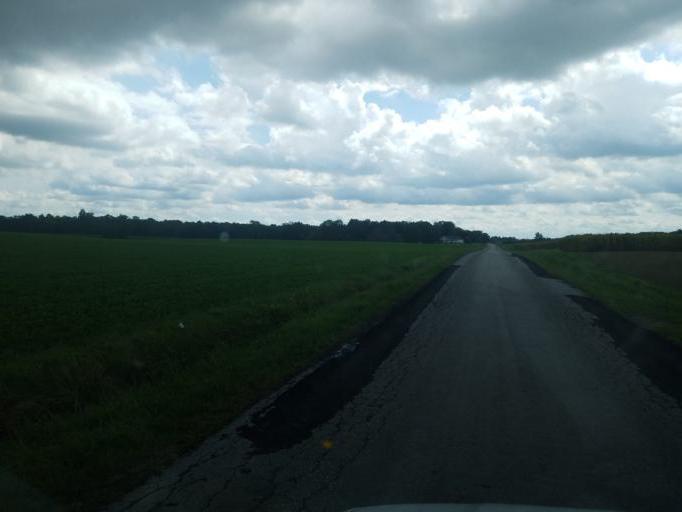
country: US
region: Ohio
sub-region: Huron County
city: Greenwich
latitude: 40.9515
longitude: -82.5259
